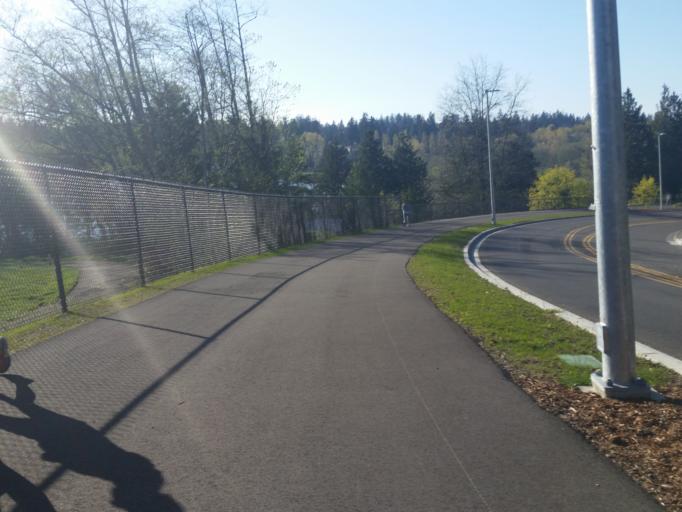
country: US
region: Washington
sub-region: Snohomish County
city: Mountlake Terrace
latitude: 47.7849
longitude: -122.3246
